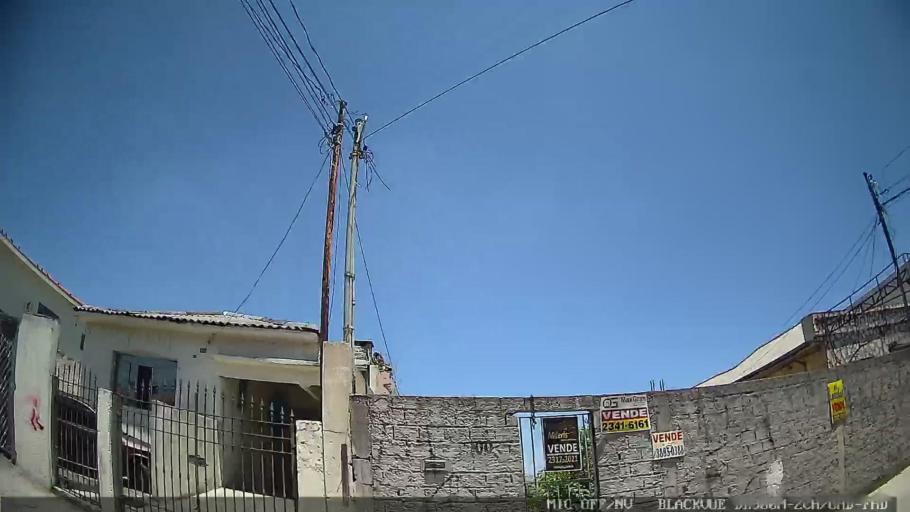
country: BR
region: Sao Paulo
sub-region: Sao Caetano Do Sul
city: Sao Caetano do Sul
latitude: -23.5961
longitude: -46.5704
